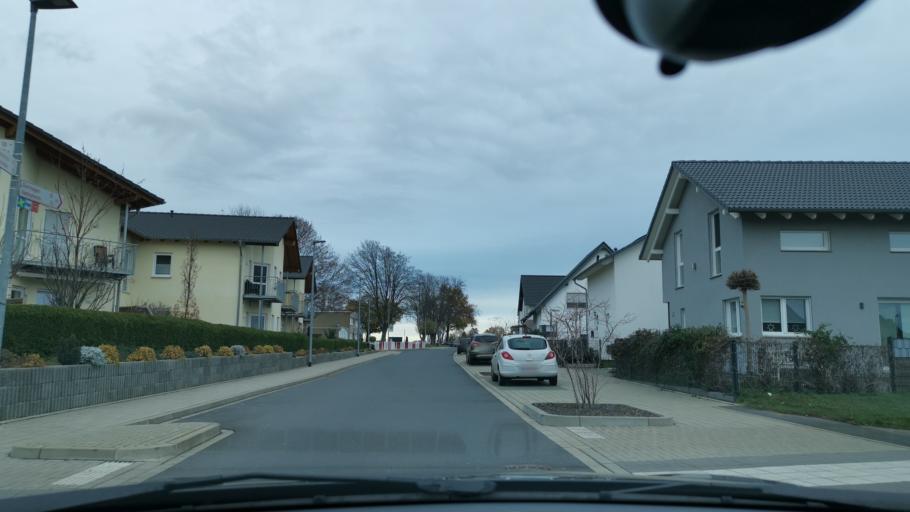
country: DE
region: North Rhine-Westphalia
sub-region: Regierungsbezirk Dusseldorf
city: Rommerskirchen
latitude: 51.0378
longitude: 6.6862
